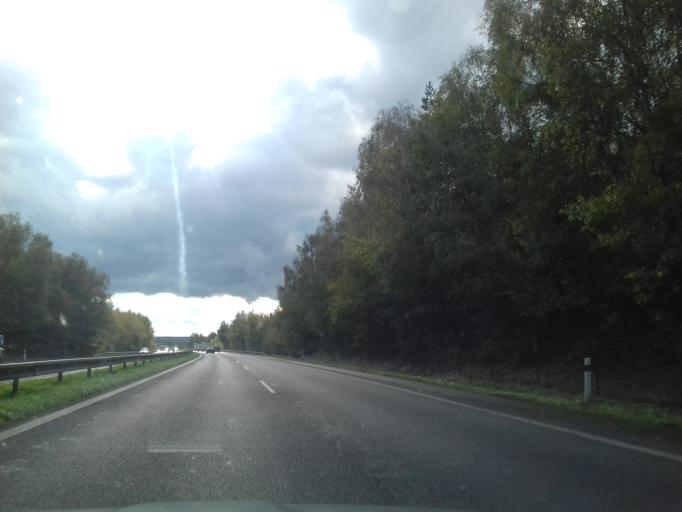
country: CZ
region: Central Bohemia
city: Benatky nad Jizerou
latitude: 50.3135
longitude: 14.8623
